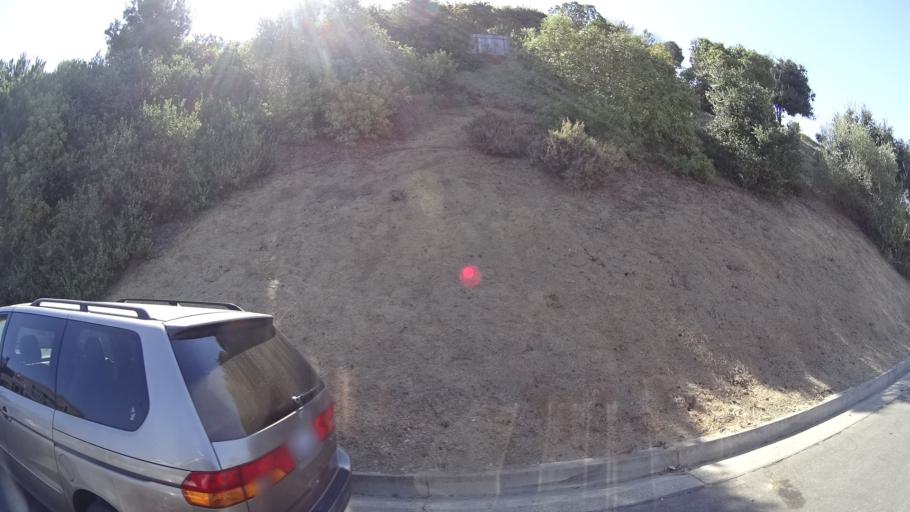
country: US
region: California
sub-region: Orange County
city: San Clemente
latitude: 33.4398
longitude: -117.6083
